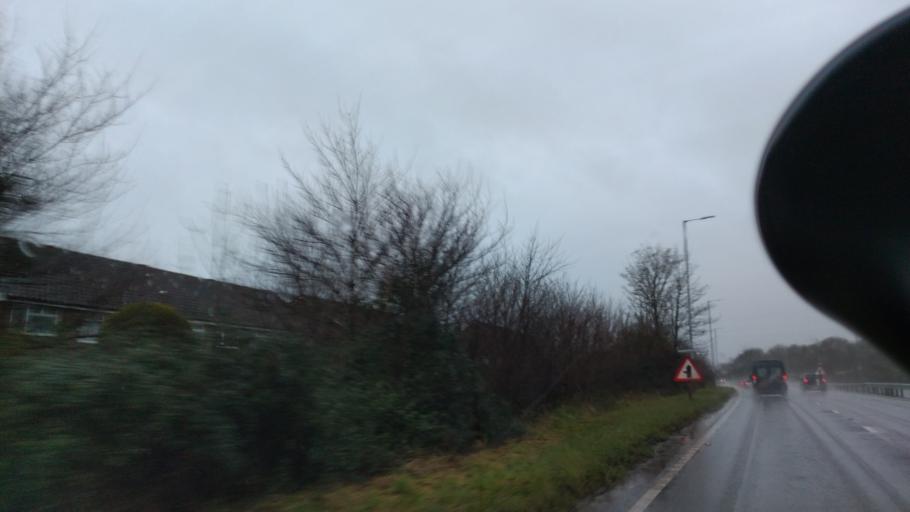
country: GB
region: England
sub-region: West Sussex
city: Lancing
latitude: 50.8377
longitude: -0.3395
